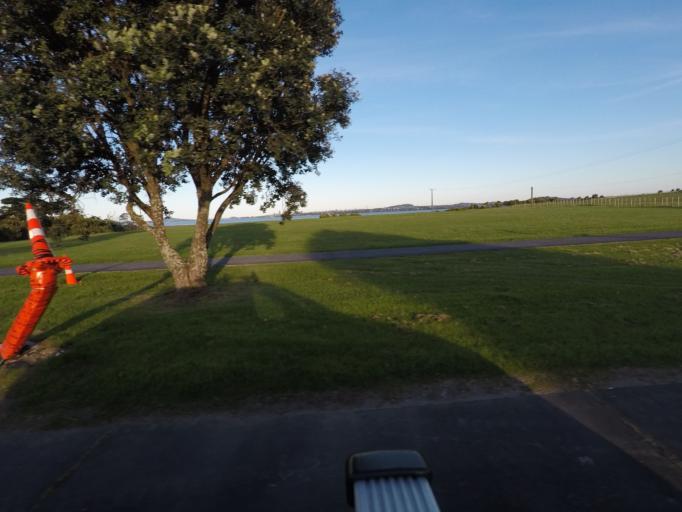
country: NZ
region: Auckland
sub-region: Auckland
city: Rosebank
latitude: -36.8513
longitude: 174.6511
